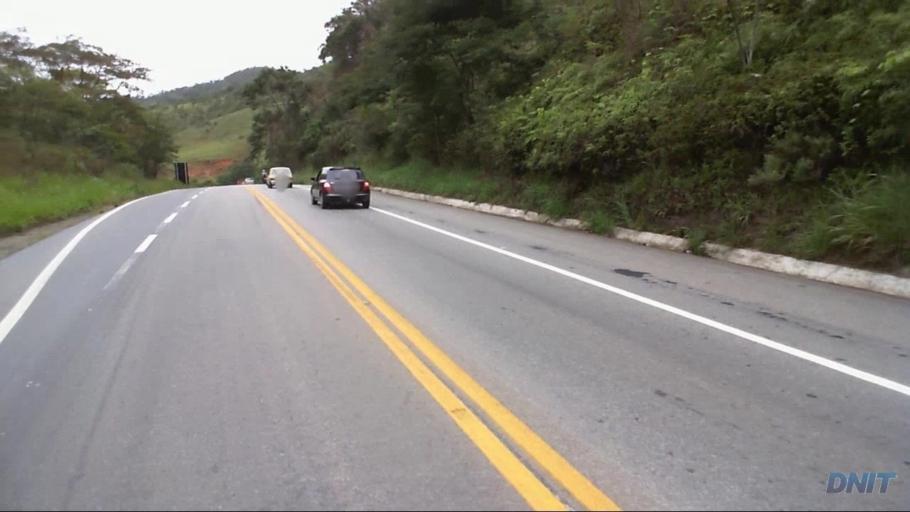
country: BR
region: Minas Gerais
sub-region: Timoteo
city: Timoteo
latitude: -19.6298
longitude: -42.8333
